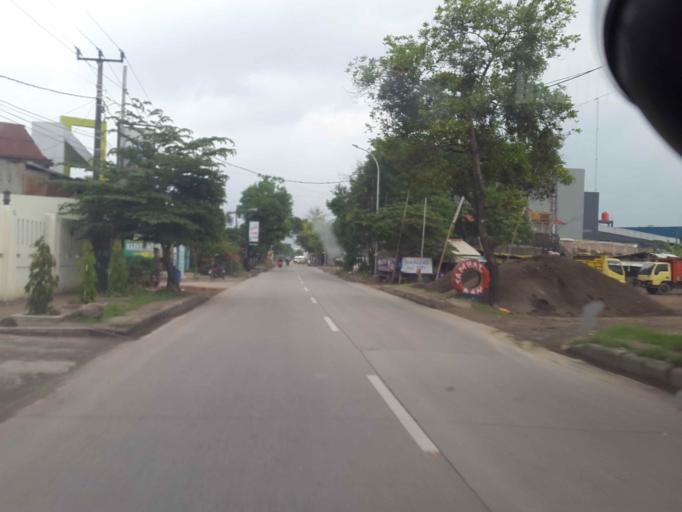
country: ID
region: West Java
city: Cikarang
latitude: -6.2869
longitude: 107.1566
